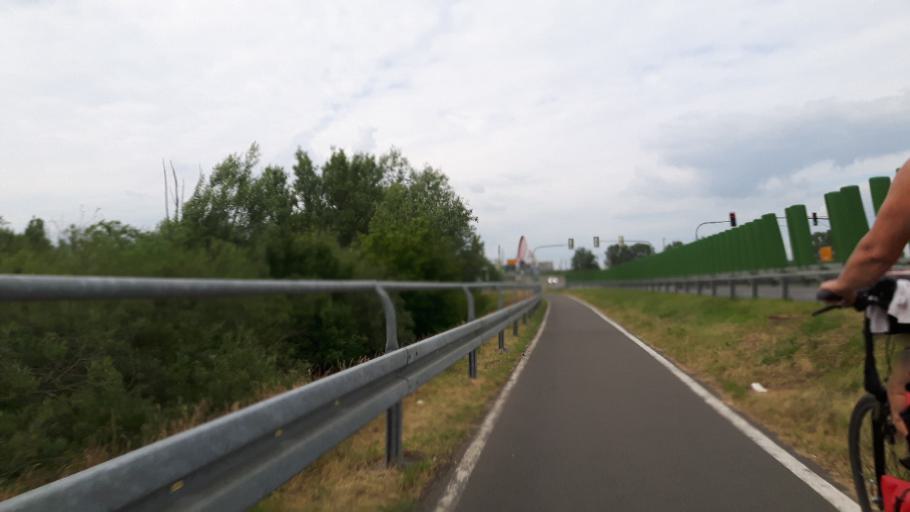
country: DE
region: Saxony-Anhalt
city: Wittenburg
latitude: 51.8517
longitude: 12.6493
